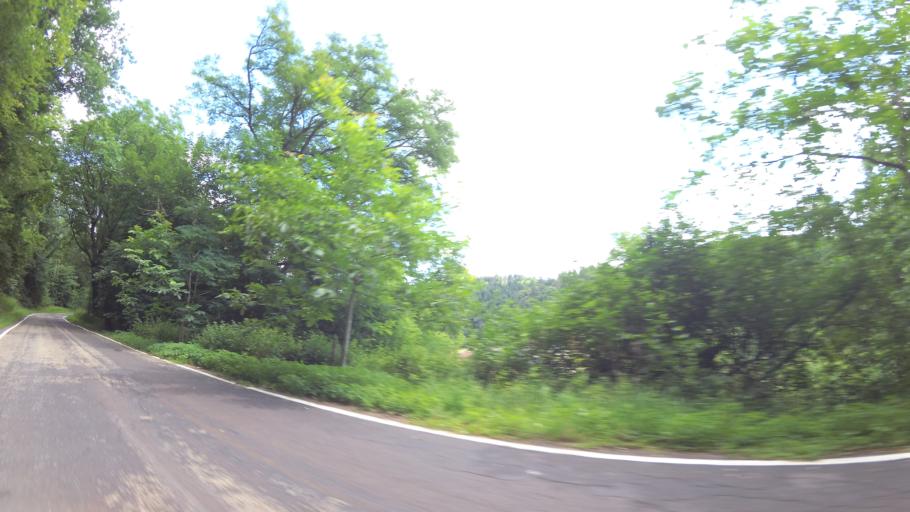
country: DE
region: Saarland
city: Wadern
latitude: 49.5336
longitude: 6.8990
